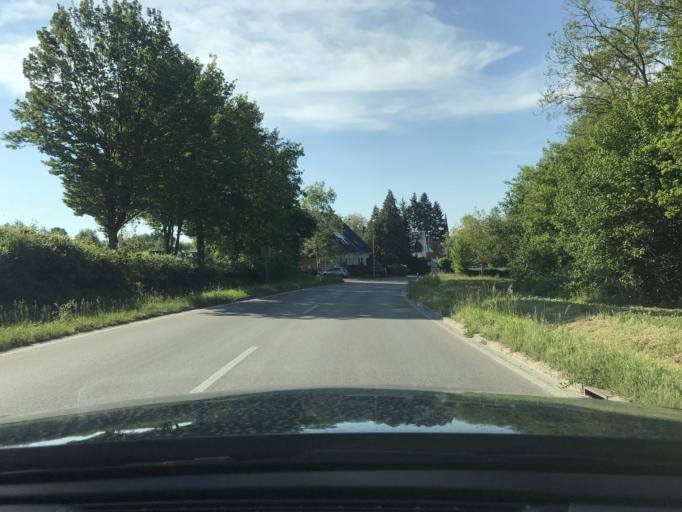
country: DE
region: Baden-Wuerttemberg
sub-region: Regierungsbezirk Stuttgart
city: Schwaikheim
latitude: 48.8827
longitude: 9.3160
